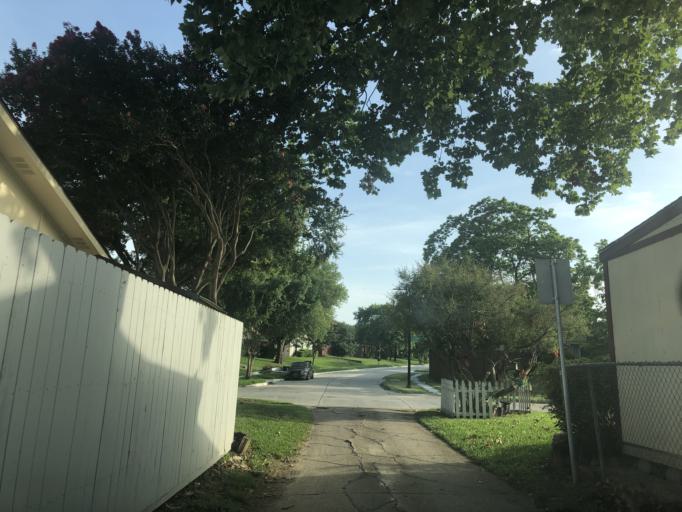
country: US
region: Texas
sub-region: Dallas County
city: Sunnyvale
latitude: 32.8344
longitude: -96.5912
